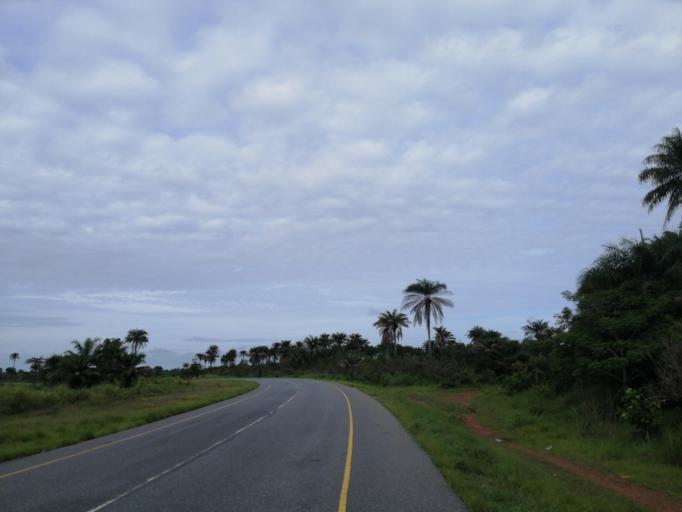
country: SL
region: Northern Province
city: Port Loko
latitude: 8.7925
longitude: -12.8465
